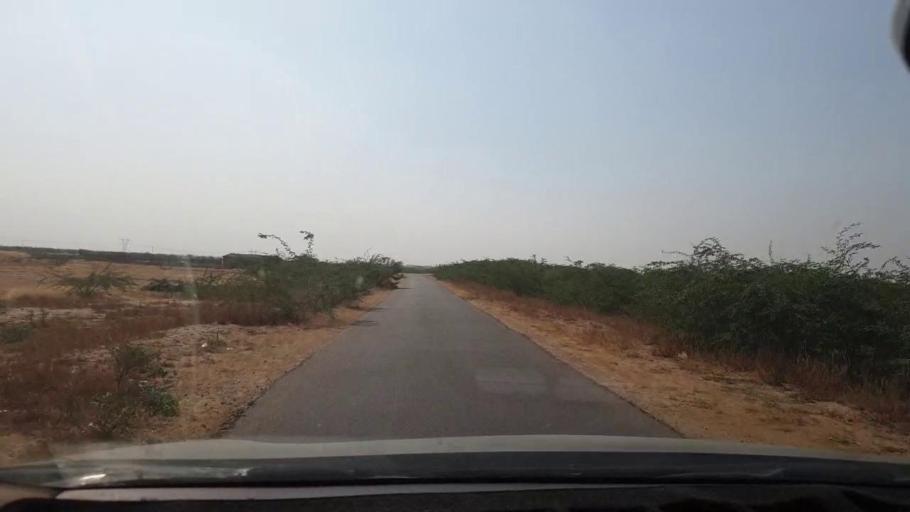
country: PK
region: Sindh
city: Malir Cantonment
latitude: 25.1255
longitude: 67.2232
